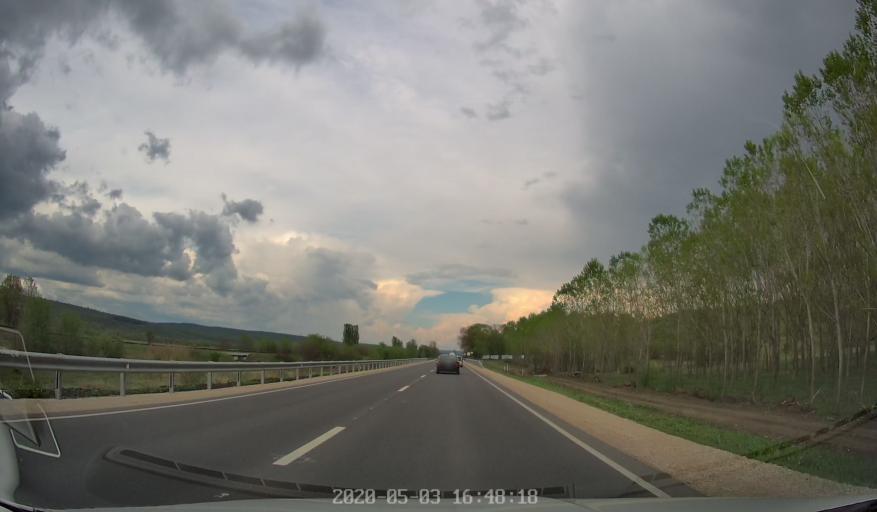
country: MD
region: Stinga Nistrului
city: Bucovat
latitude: 47.1791
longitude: 28.4929
